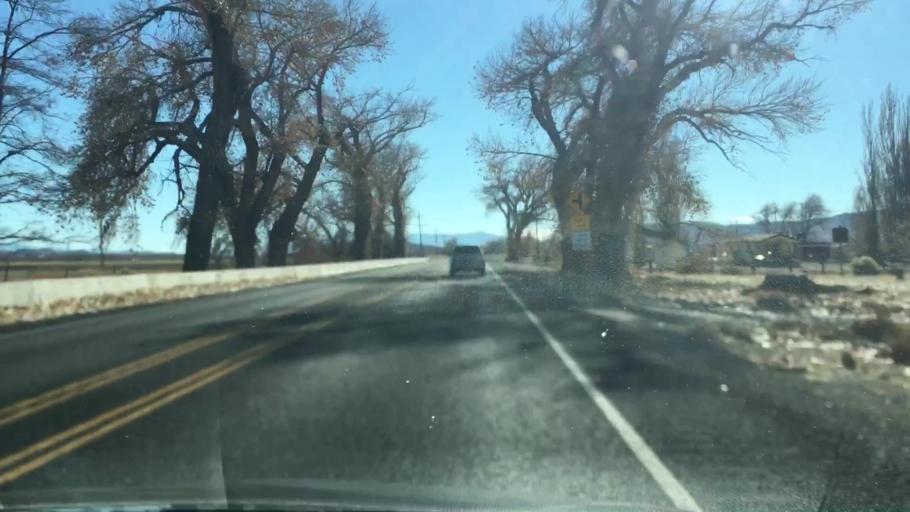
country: US
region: Nevada
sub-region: Lyon County
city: Yerington
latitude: 39.0499
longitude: -119.1815
